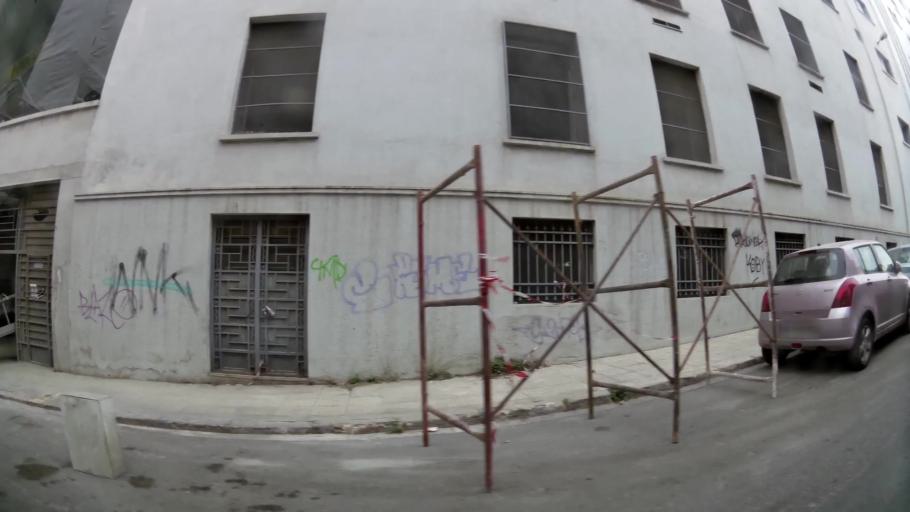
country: GR
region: Attica
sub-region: Nomos Attikis
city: Piraeus
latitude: 37.9522
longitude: 23.6418
